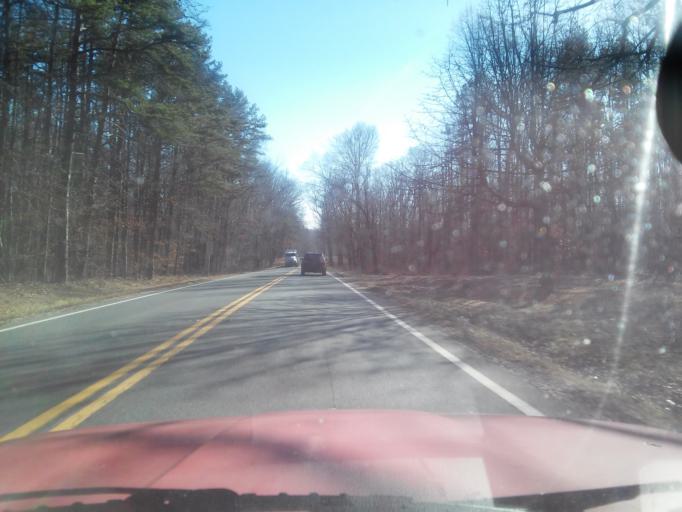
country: US
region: Virginia
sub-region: Orange County
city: Gordonsville
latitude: 38.0065
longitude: -78.1919
